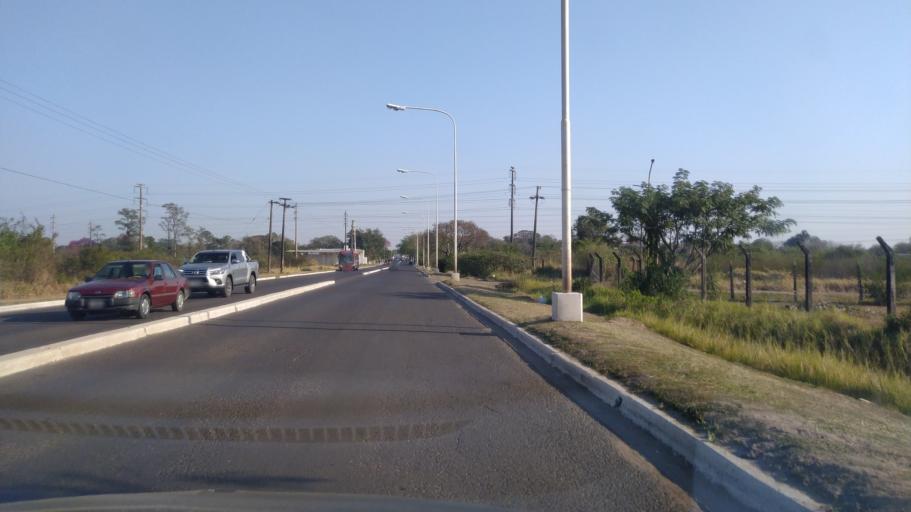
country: AR
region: Corrientes
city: Corrientes
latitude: -27.5168
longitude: -58.8038
